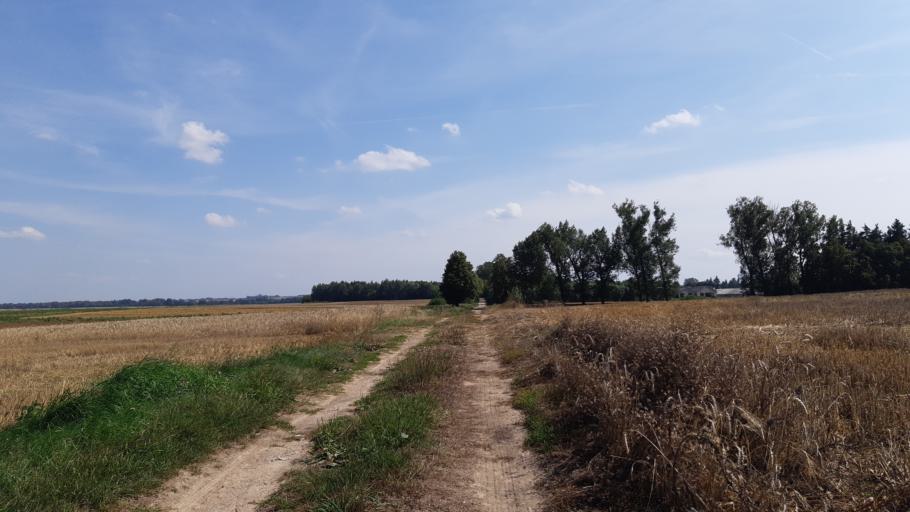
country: LT
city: Virbalis
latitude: 54.6414
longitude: 22.8198
